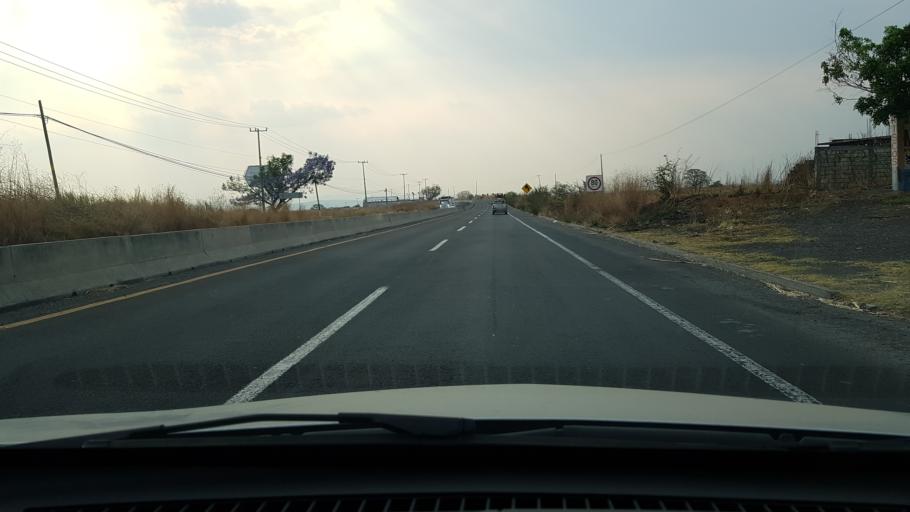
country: MX
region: Morelos
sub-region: Ayala
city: Unidad Habitacional Mariano Matamoros
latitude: 18.7541
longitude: -98.8581
